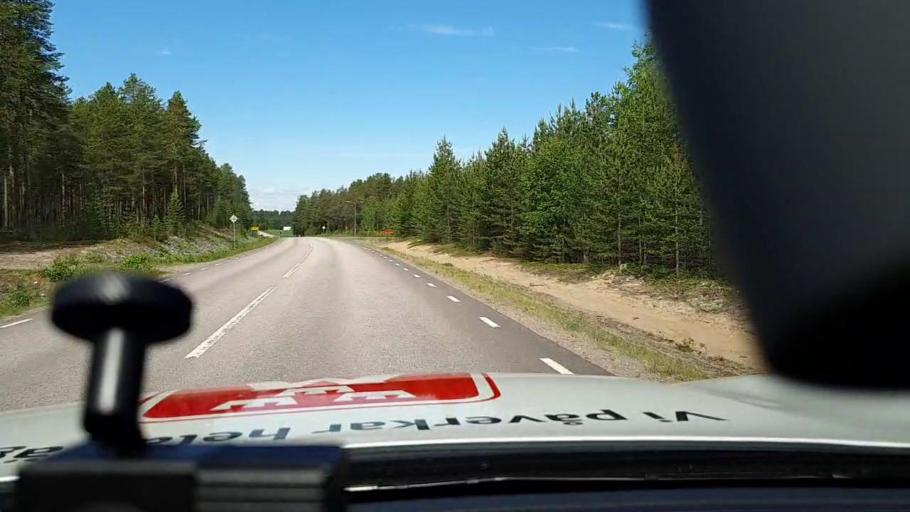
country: SE
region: Norrbotten
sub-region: Lulea Kommun
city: Sodra Sunderbyn
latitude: 65.6346
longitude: 21.9198
